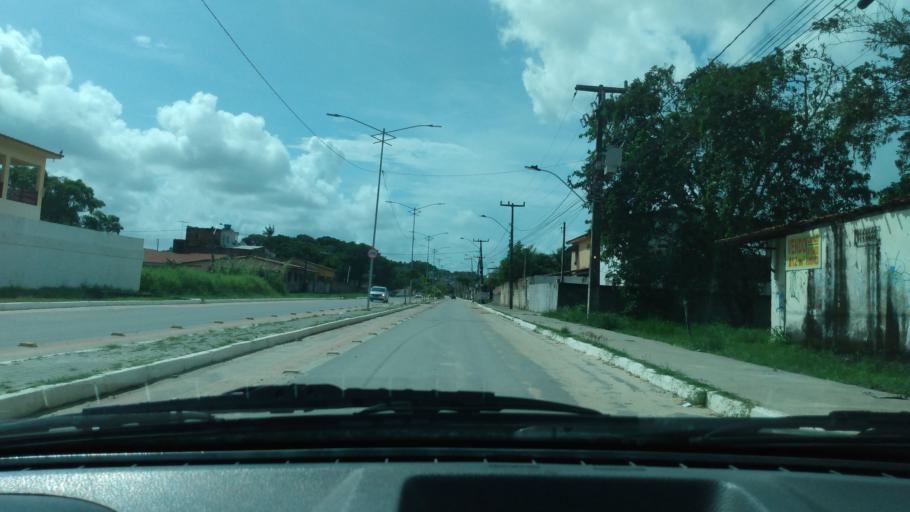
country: BR
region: Pernambuco
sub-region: Cabo De Santo Agostinho
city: Cabo
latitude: -8.3255
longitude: -34.9534
